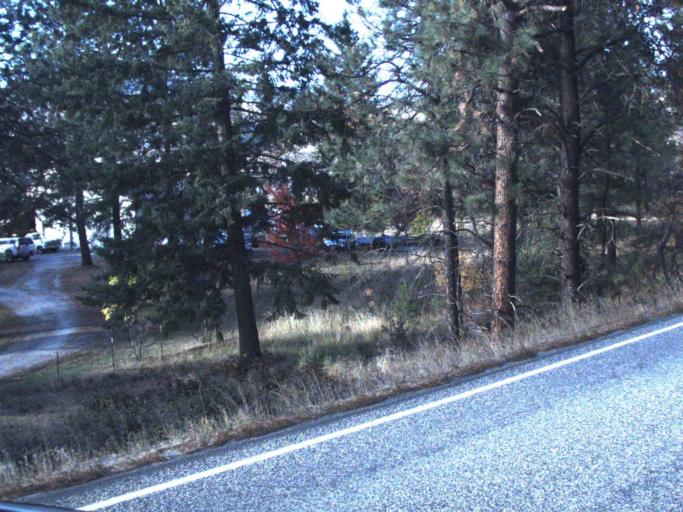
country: CA
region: British Columbia
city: Rossland
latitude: 48.8577
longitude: -117.8785
